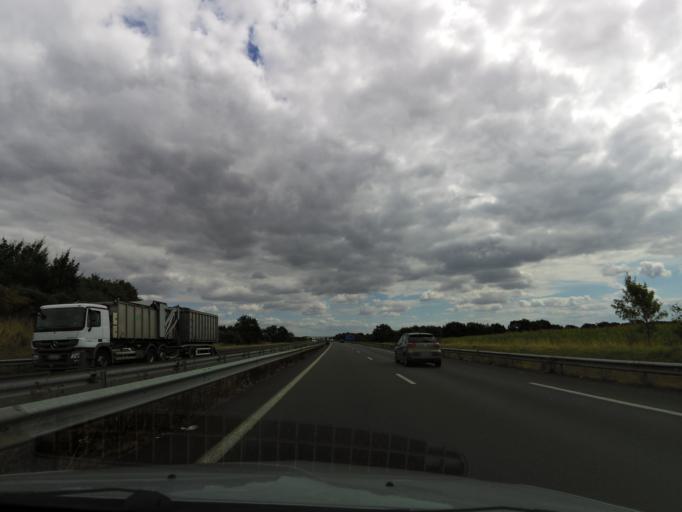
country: FR
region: Pays de la Loire
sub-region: Departement de la Loire-Atlantique
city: Le Bignon
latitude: 47.1074
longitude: -1.4845
